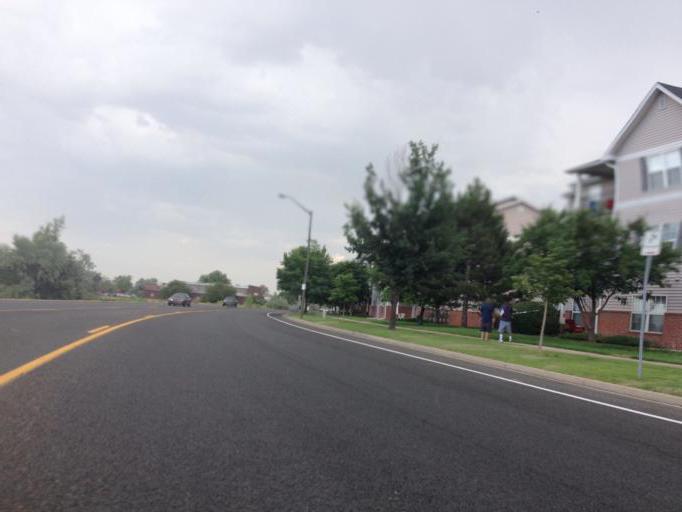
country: US
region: Colorado
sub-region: Larimer County
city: Fort Collins
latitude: 40.5887
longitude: -105.0561
